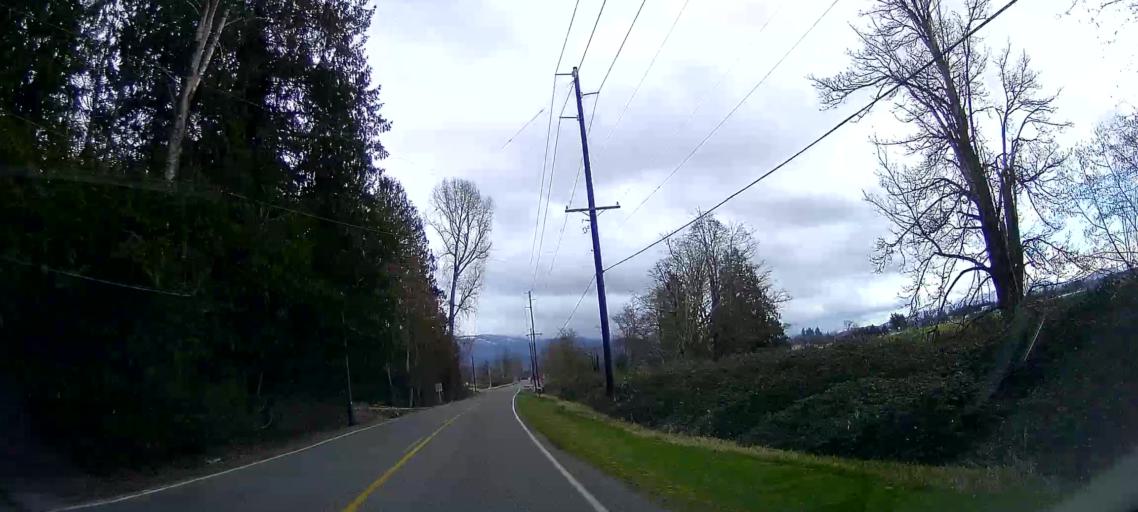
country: US
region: Washington
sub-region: Skagit County
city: Sedro-Woolley
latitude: 48.5305
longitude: -122.2820
